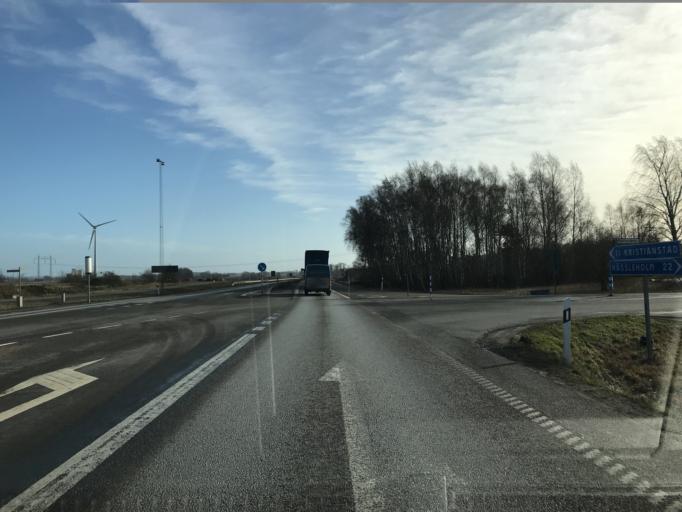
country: SE
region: Skane
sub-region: Kristianstads Kommun
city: Onnestad
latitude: 56.0393
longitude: 14.0392
